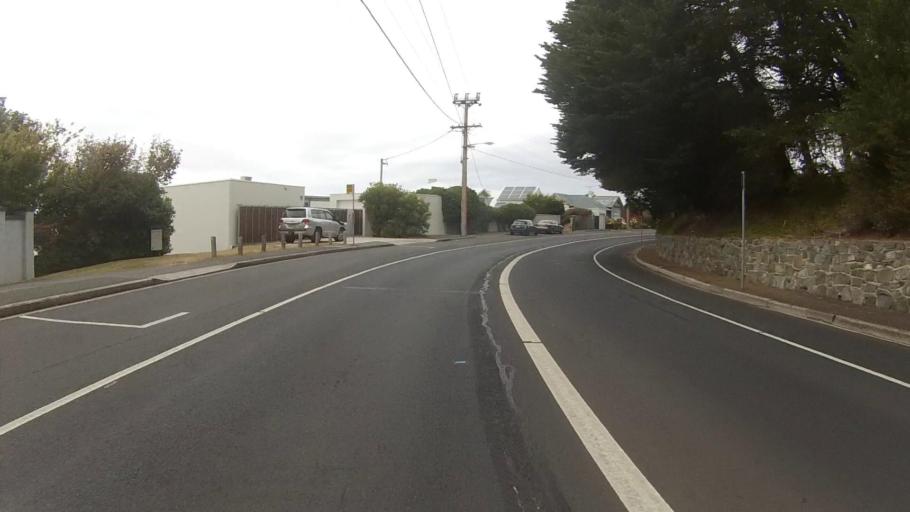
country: AU
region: Tasmania
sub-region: Kingborough
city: Taroona
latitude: -42.9268
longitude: 147.3607
